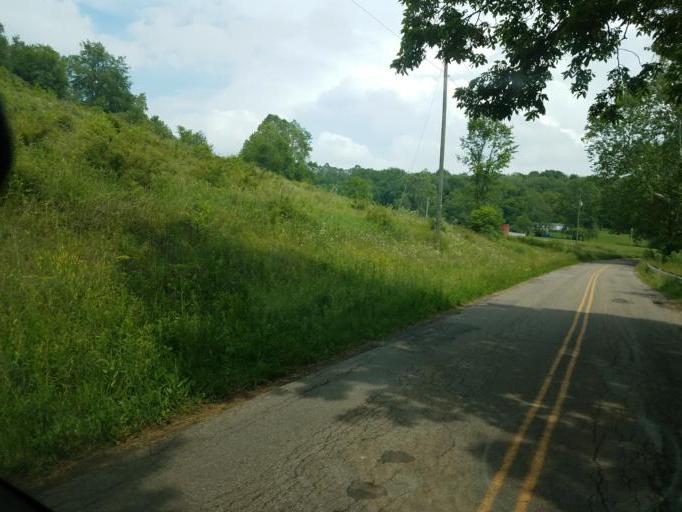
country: US
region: Ohio
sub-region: Knox County
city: Oak Hill
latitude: 40.2814
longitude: -82.2750
